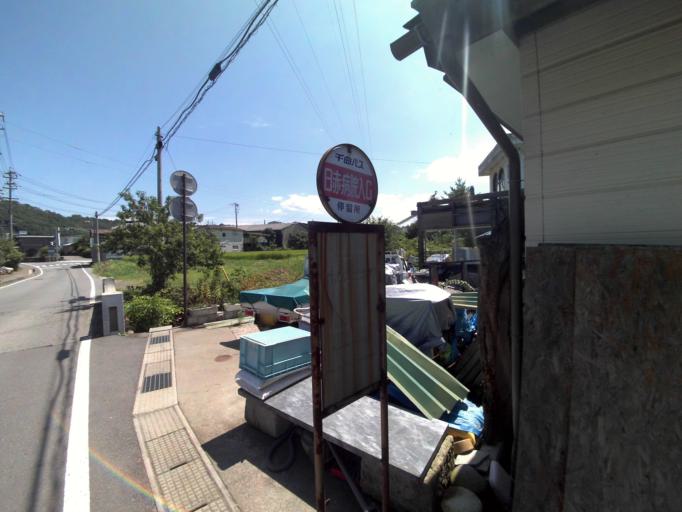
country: JP
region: Nagano
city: Komoro
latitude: 36.2680
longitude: 138.3568
